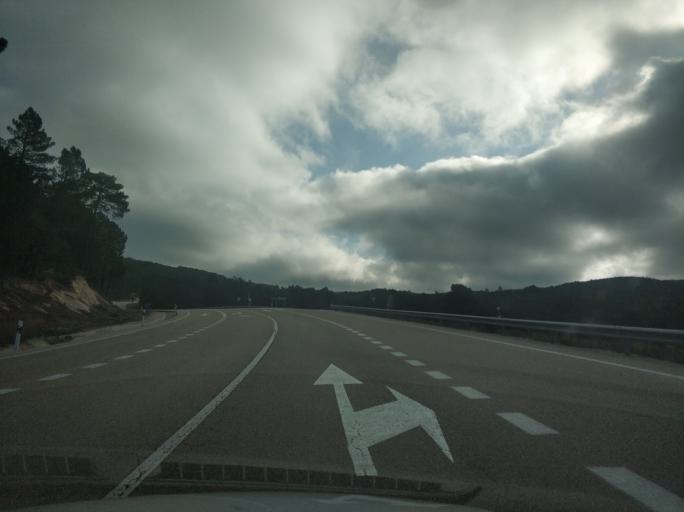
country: ES
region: Castille and Leon
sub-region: Provincia de Soria
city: Navaleno
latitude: 41.8321
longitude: -2.9900
